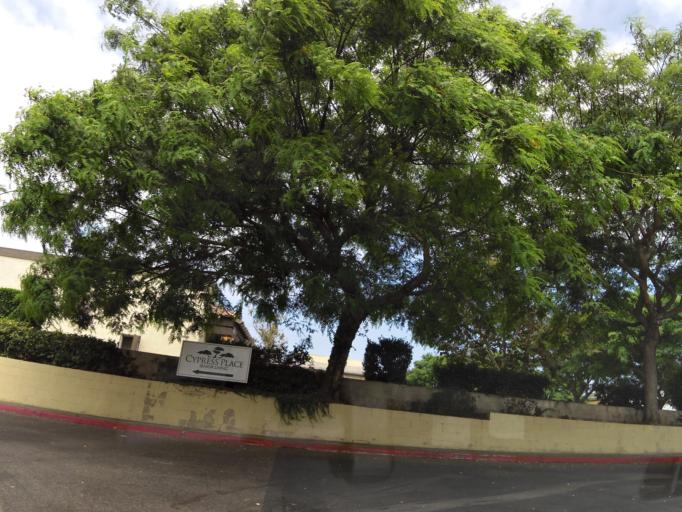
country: US
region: California
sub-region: Ventura County
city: El Rio
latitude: 34.2639
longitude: -119.2131
